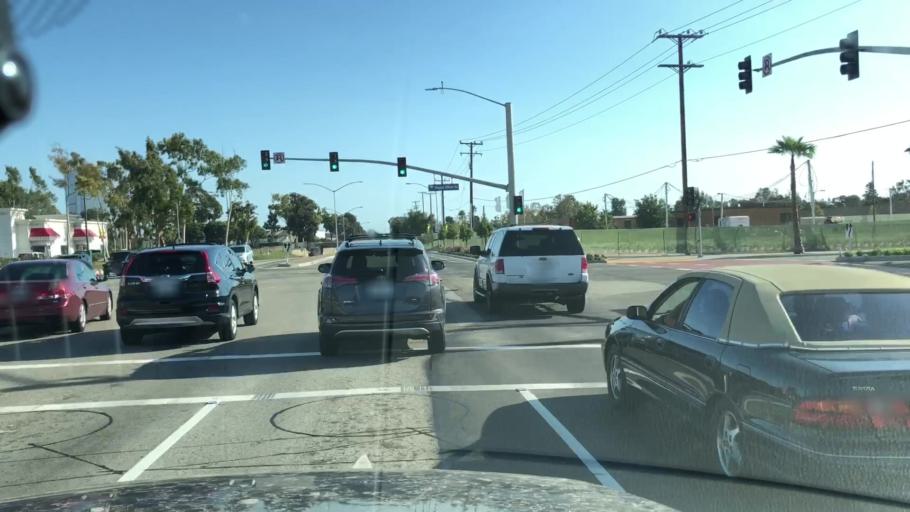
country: US
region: California
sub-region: Ventura County
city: El Rio
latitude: 34.2360
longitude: -119.1805
